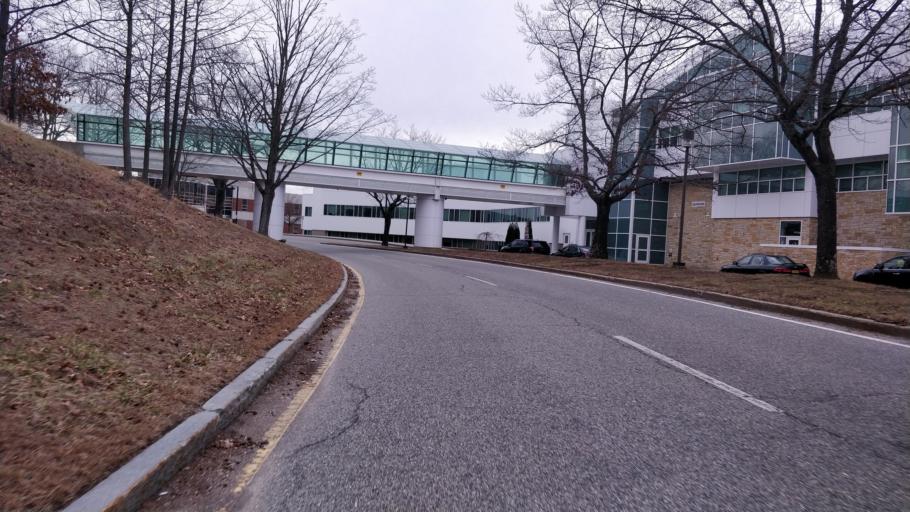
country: US
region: New York
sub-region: Nassau County
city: Brookville
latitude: 40.7997
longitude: -73.5739
